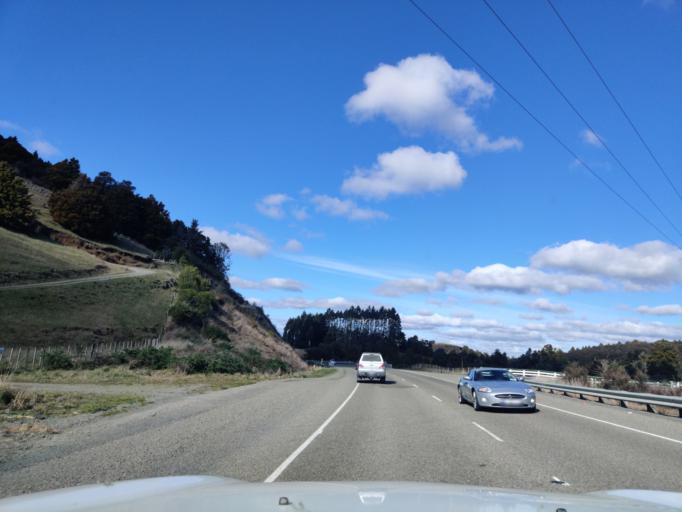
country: NZ
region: Manawatu-Wanganui
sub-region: Ruapehu District
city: Waiouru
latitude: -39.5774
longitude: 175.7142
